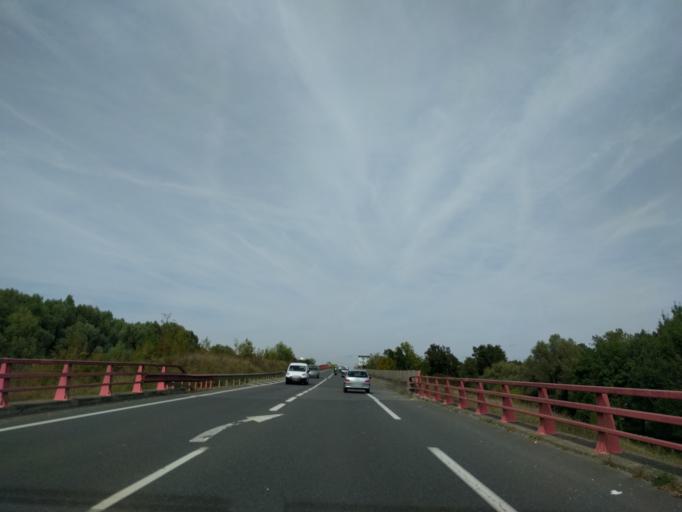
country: FR
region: Centre
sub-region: Departement du Cher
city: Saint-Germain-du-Puy
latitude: 47.0908
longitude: 2.4433
